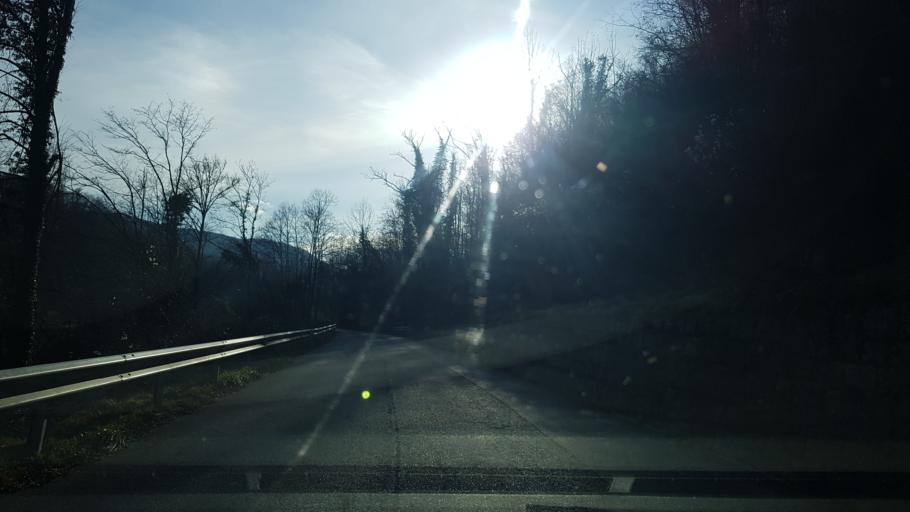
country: IT
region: Friuli Venezia Giulia
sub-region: Provincia di Udine
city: Merso di Sopra
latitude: 46.1384
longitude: 13.5396
